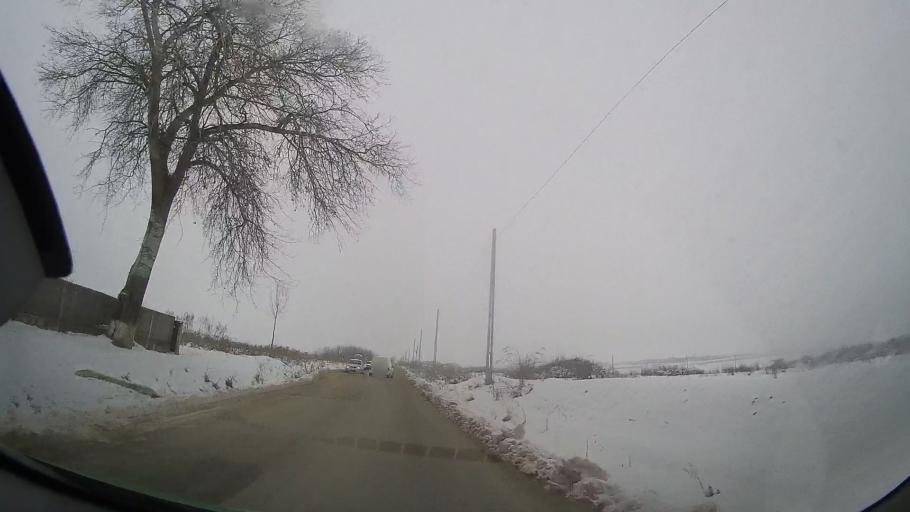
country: RO
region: Vaslui
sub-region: Comuna Todiresti
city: Todiresti
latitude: 46.8517
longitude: 27.3943
